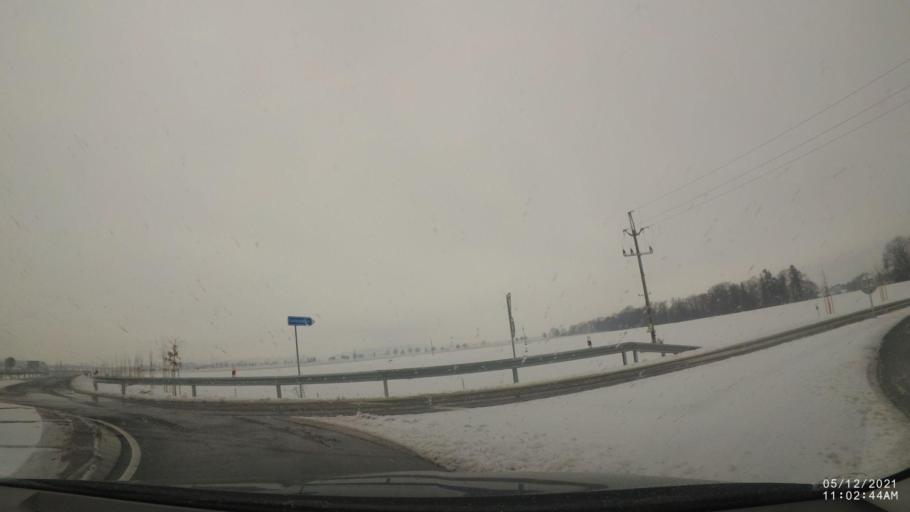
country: CZ
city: Solnice
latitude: 50.1831
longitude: 16.2196
